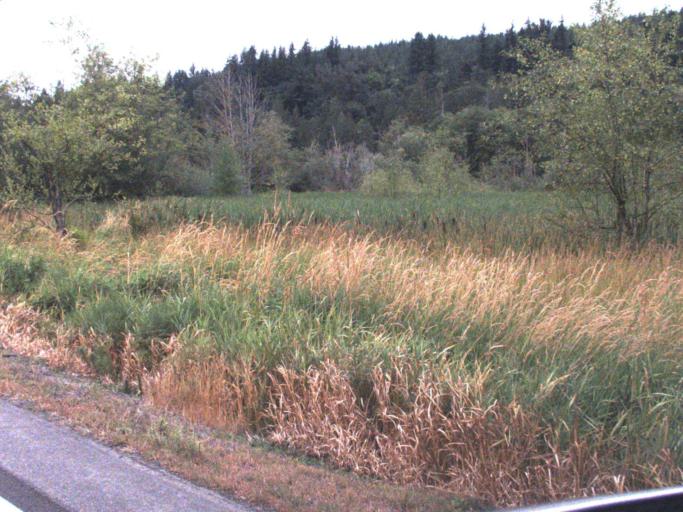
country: US
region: Washington
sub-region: King County
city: Fall City
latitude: 47.5898
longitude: -121.9048
